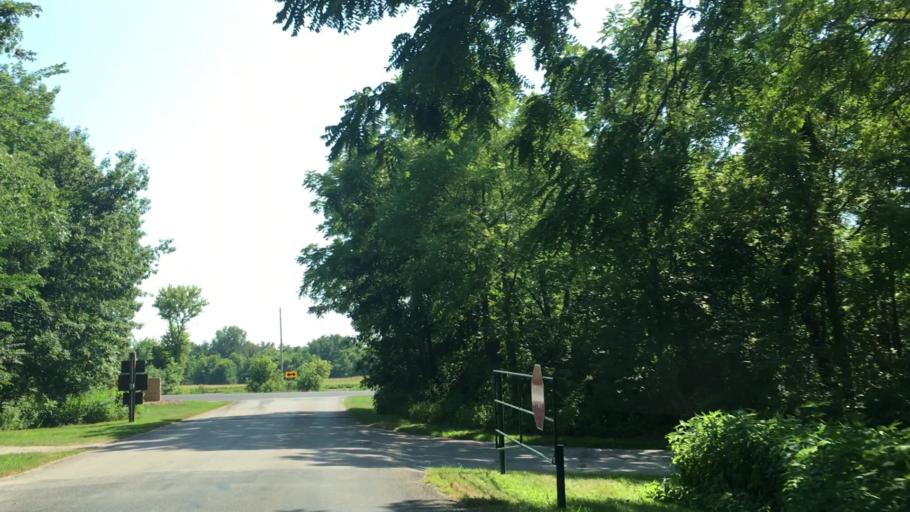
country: US
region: Iowa
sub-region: Johnson County
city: Tiffin
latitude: 41.7186
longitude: -91.7303
